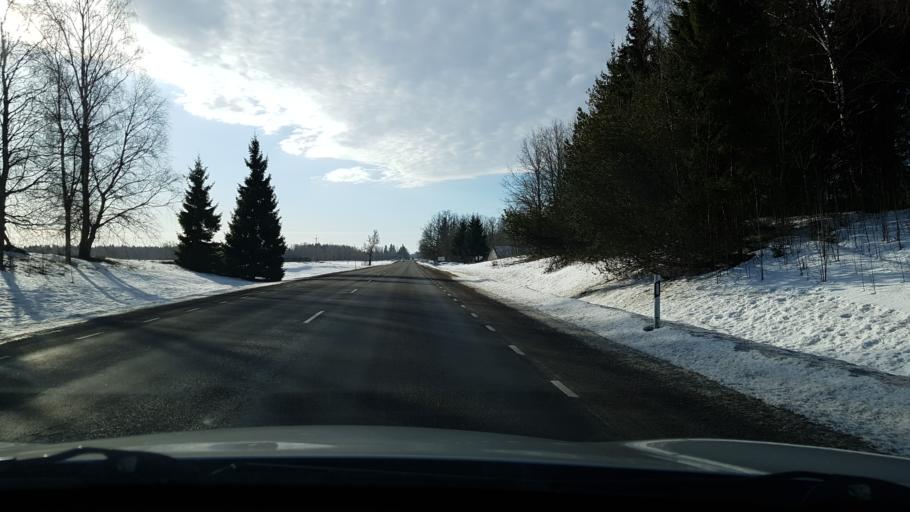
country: EE
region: Viljandimaa
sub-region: Viljandi linn
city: Viljandi
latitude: 58.4466
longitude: 25.5957
